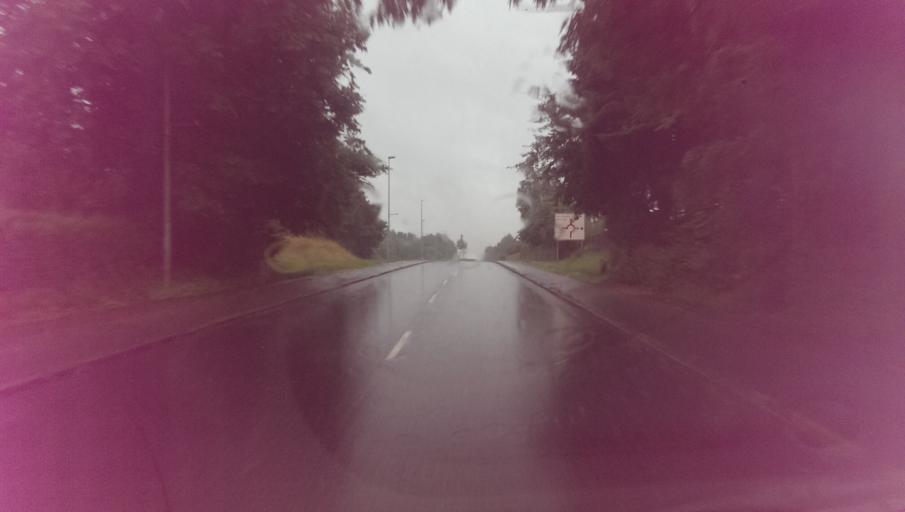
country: DK
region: Central Jutland
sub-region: Silkeborg Kommune
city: Virklund
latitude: 56.0918
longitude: 9.5477
